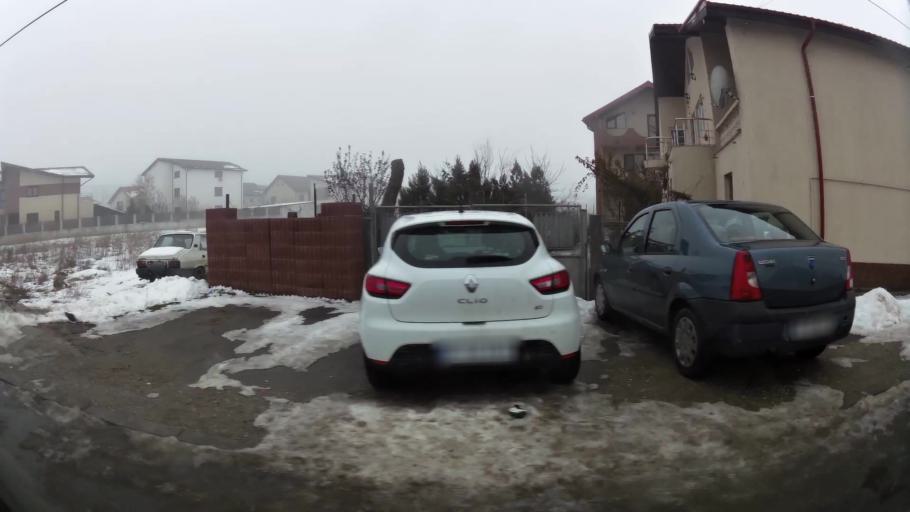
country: RO
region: Ilfov
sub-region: Comuna Chiajna
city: Chiajna
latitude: 44.4549
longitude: 25.9842
